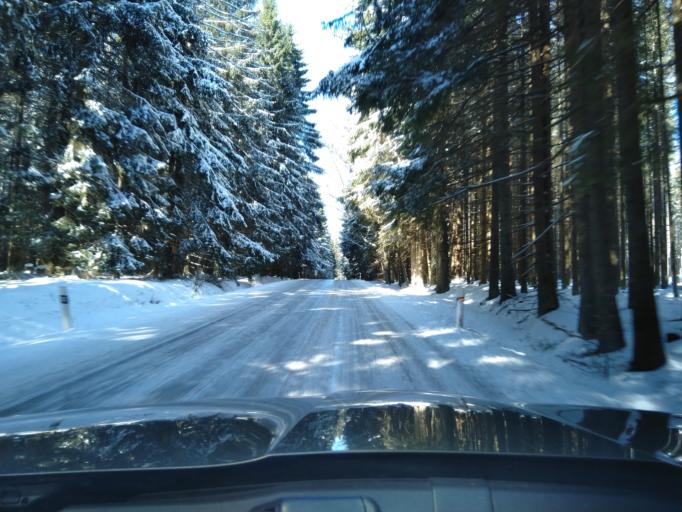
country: CZ
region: Jihocesky
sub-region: Okres Prachatice
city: Stachy
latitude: 49.0572
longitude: 13.6499
